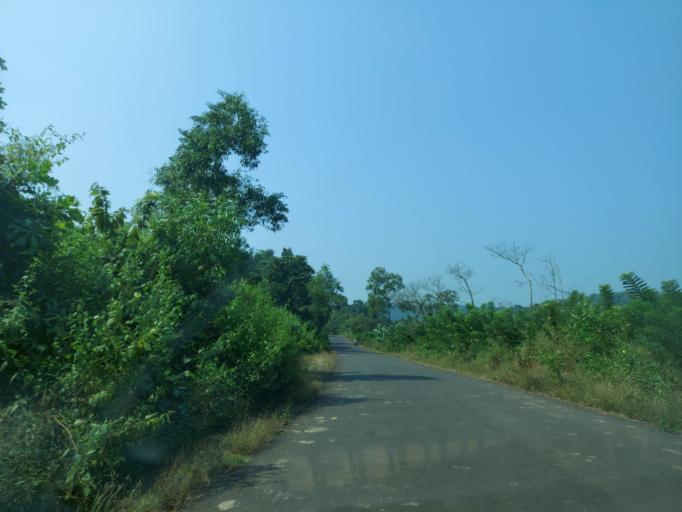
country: IN
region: Maharashtra
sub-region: Sindhudurg
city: Kudal
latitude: 15.9772
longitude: 73.6144
